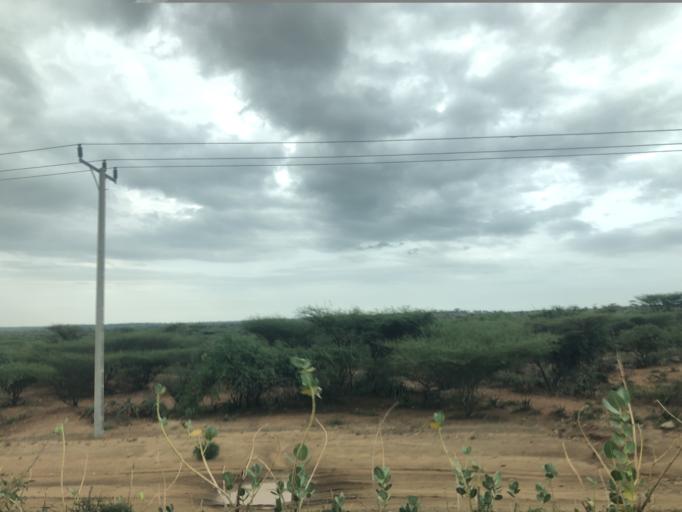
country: ET
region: Southern Nations, Nationalities, and People's Region
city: Turmi
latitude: 5.0167
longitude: 36.4856
